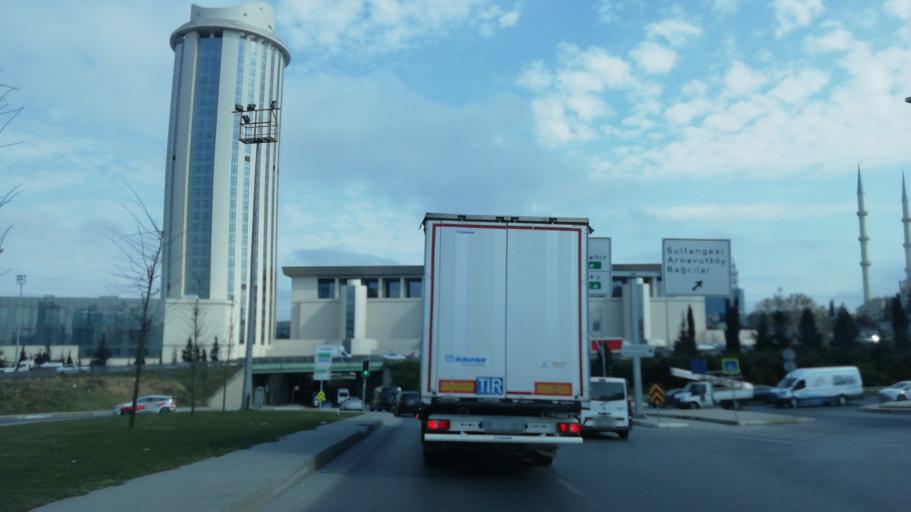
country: TR
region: Istanbul
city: Mahmutbey
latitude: 41.0623
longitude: 28.8251
